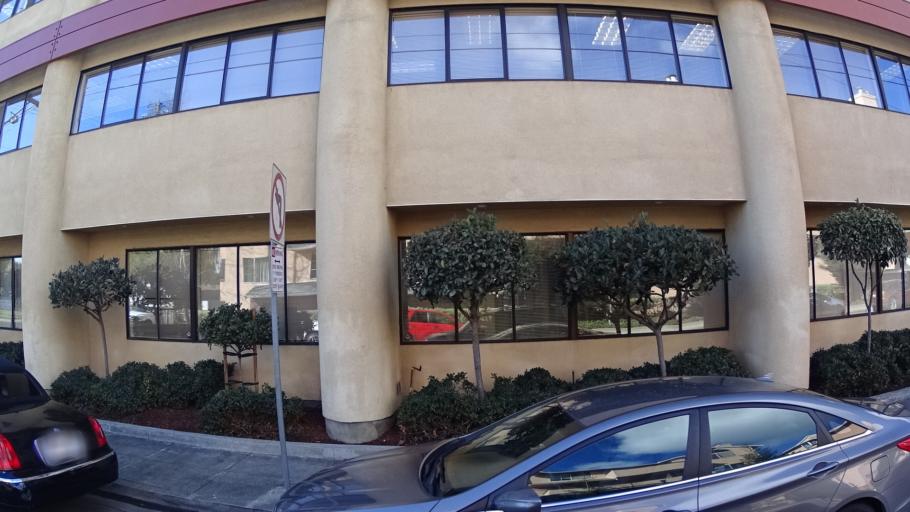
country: US
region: California
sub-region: Alameda County
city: Hayward
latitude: 37.6767
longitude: -122.0780
